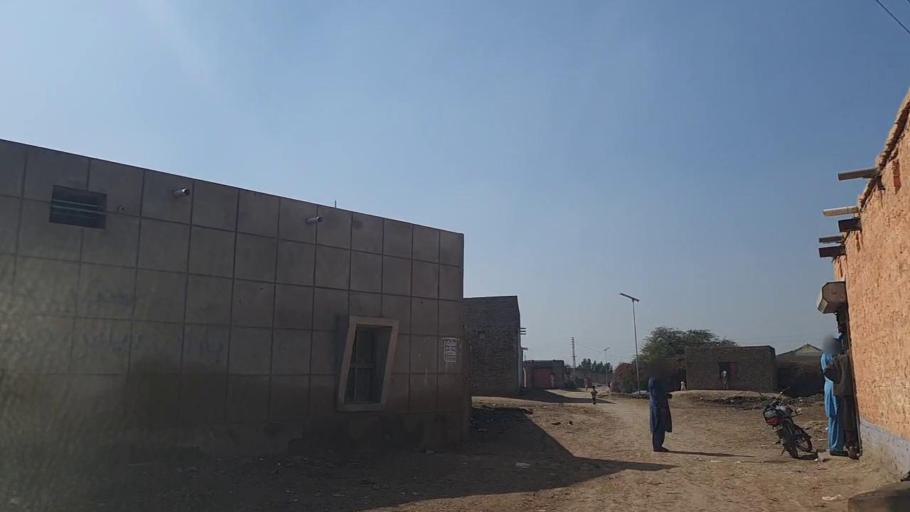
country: PK
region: Sindh
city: Shahpur Chakar
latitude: 26.1944
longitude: 68.5523
